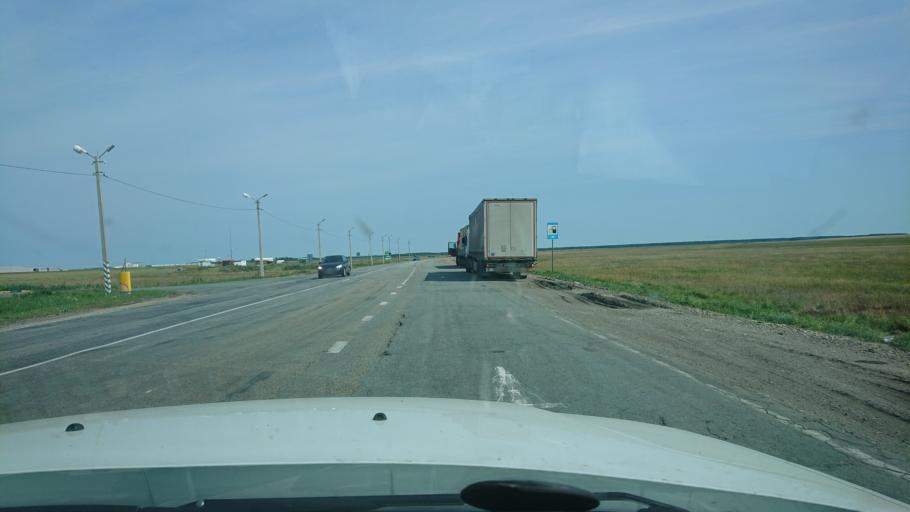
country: RU
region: Tjumen
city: Armizonskoye
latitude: 55.5360
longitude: 67.8945
